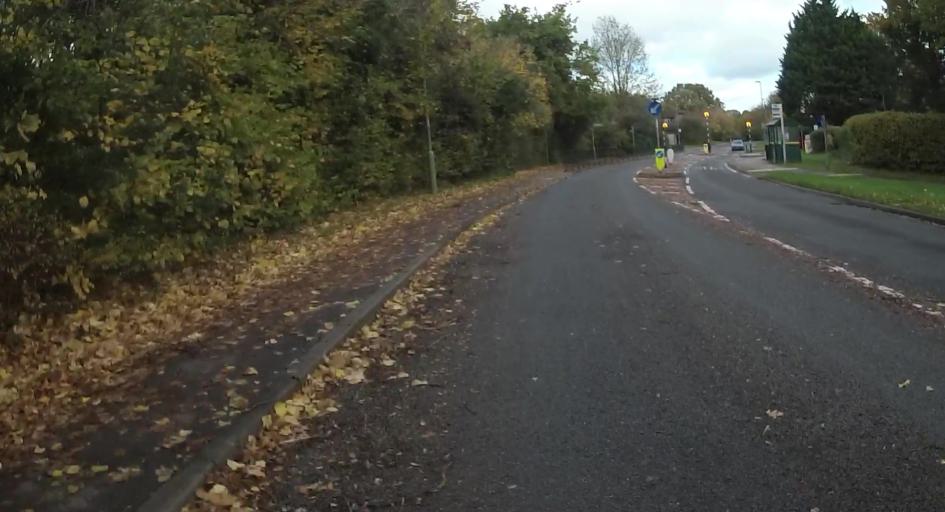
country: GB
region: England
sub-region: Hampshire
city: Old Basing
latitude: 51.2919
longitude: -1.0539
